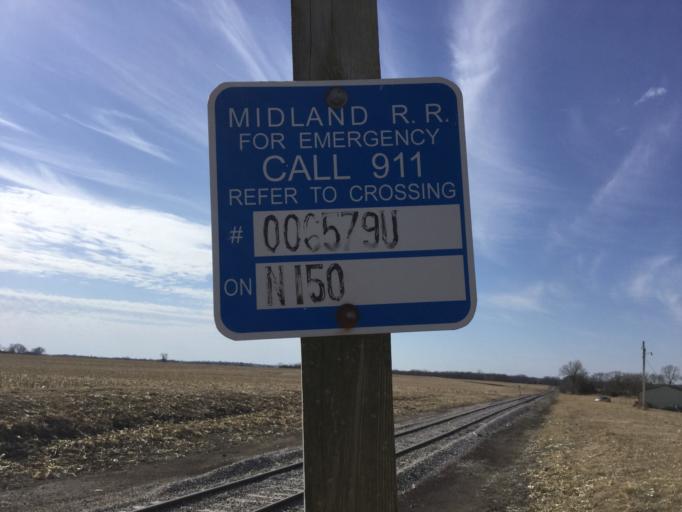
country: US
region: Kansas
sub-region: Douglas County
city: Baldwin City
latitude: 38.7605
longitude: -95.2165
